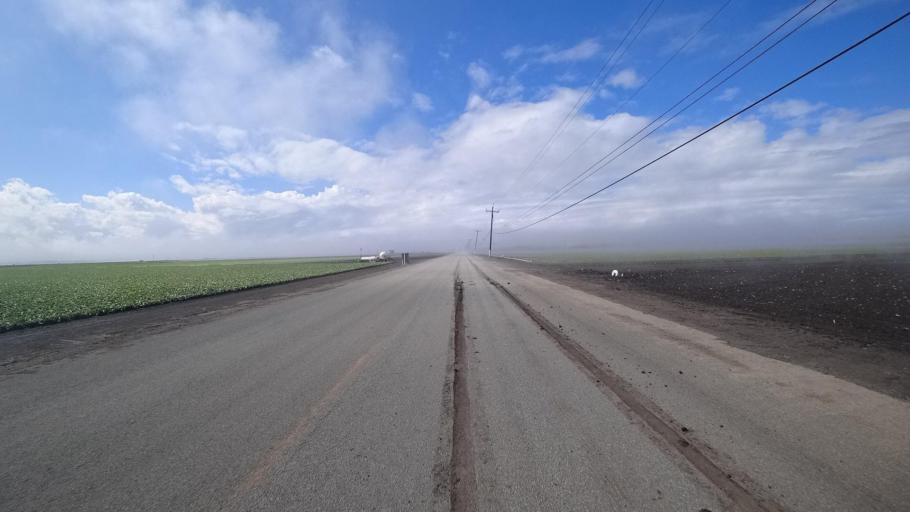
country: US
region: California
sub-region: Monterey County
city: Castroville
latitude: 36.7788
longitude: -121.7813
